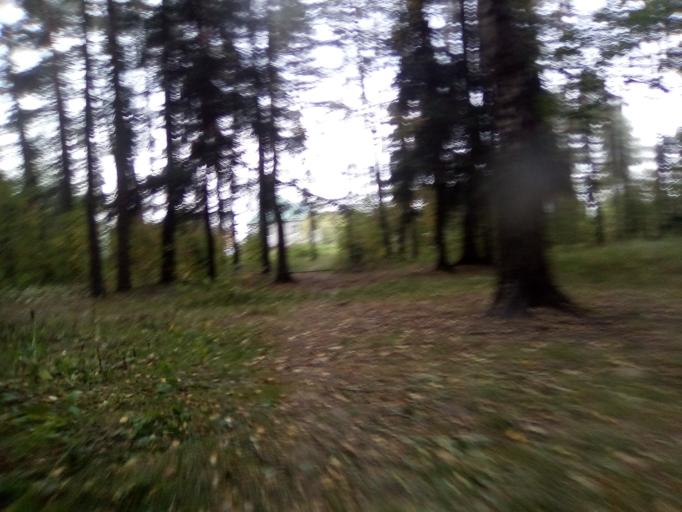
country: RU
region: Moskovskaya
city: Kokoshkino
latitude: 55.6130
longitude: 37.1853
